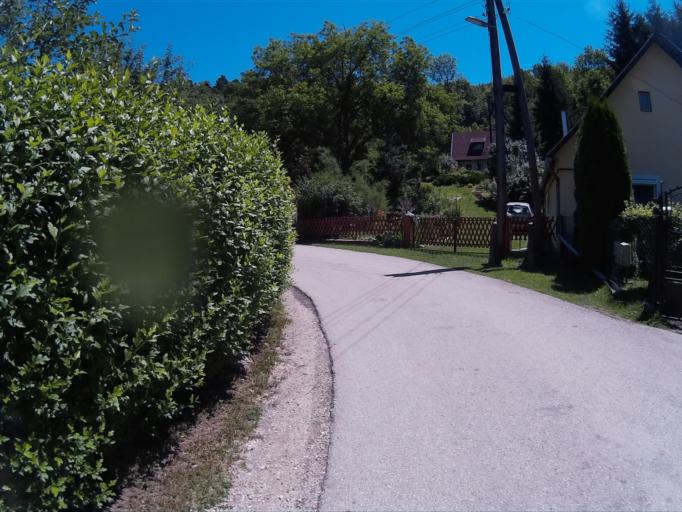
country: HU
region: Veszprem
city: Urkut
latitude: 47.1381
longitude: 17.6453
